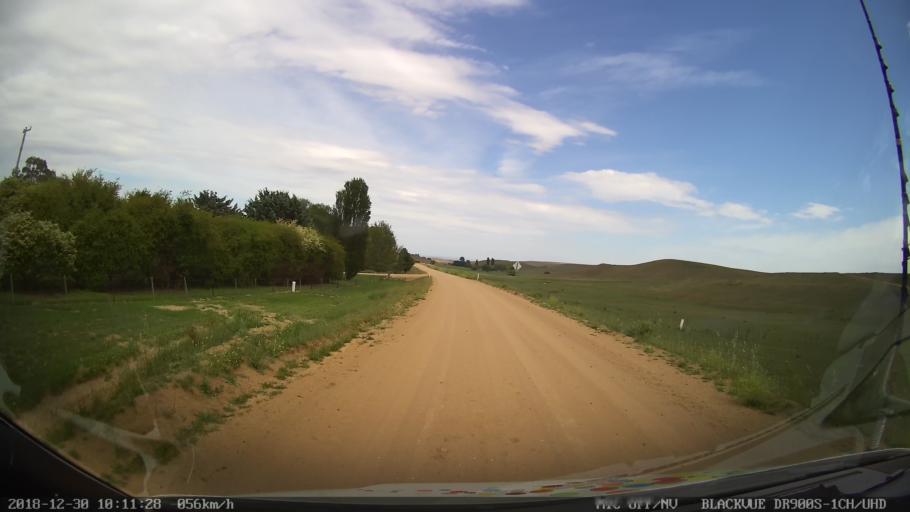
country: AU
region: New South Wales
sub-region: Cooma-Monaro
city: Cooma
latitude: -36.5469
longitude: 149.0850
